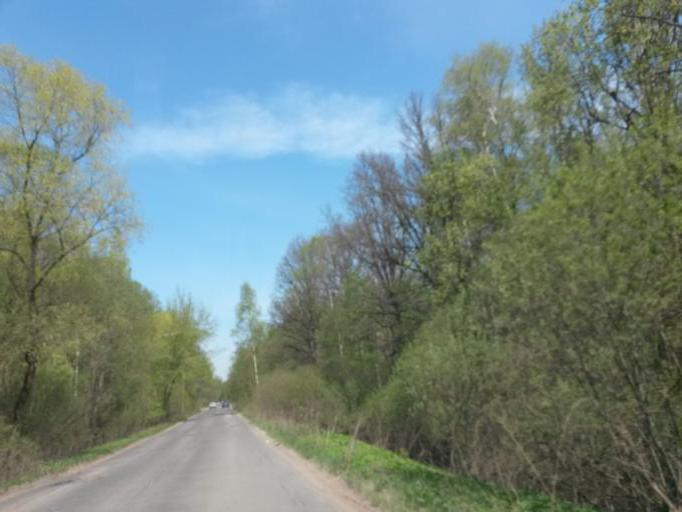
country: RU
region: Moskovskaya
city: Lyubuchany
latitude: 55.3098
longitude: 37.6155
